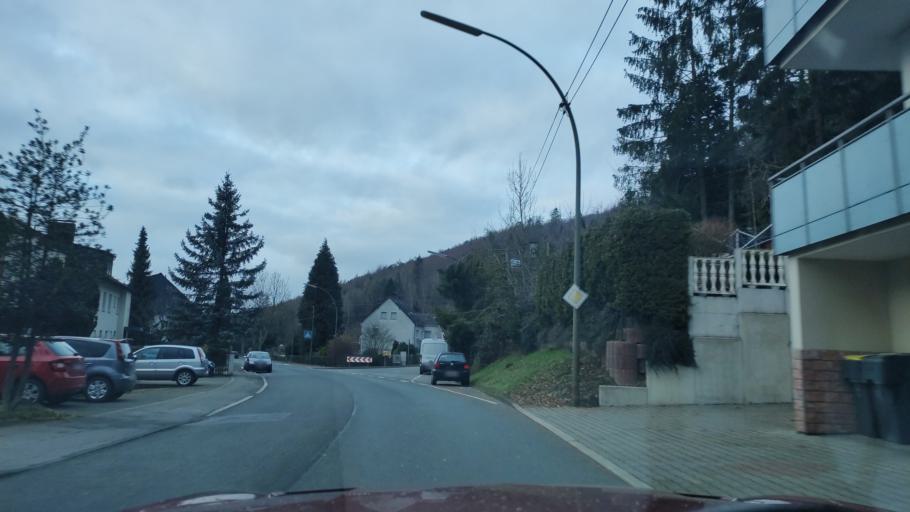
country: DE
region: North Rhine-Westphalia
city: Iserlohn
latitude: 51.3553
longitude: 7.6854
